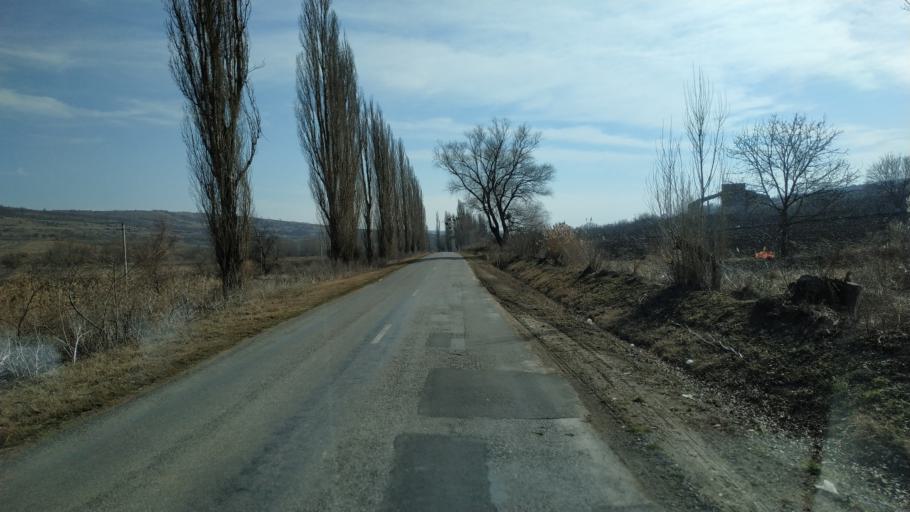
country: MD
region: Nisporeni
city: Nisporeni
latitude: 47.1639
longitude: 28.1011
